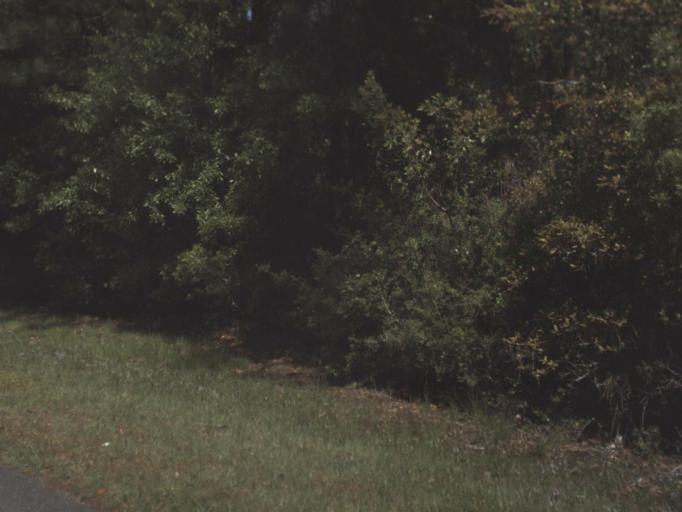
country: US
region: Florida
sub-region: Escambia County
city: Myrtle Grove
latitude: 30.4219
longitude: -87.3311
